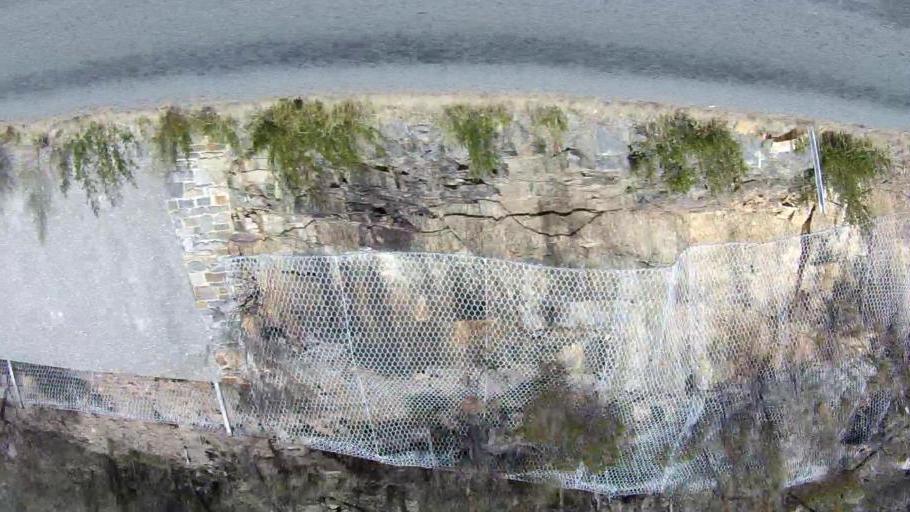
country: AU
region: Tasmania
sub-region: Sorell
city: Sorell
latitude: -42.5603
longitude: 147.8458
